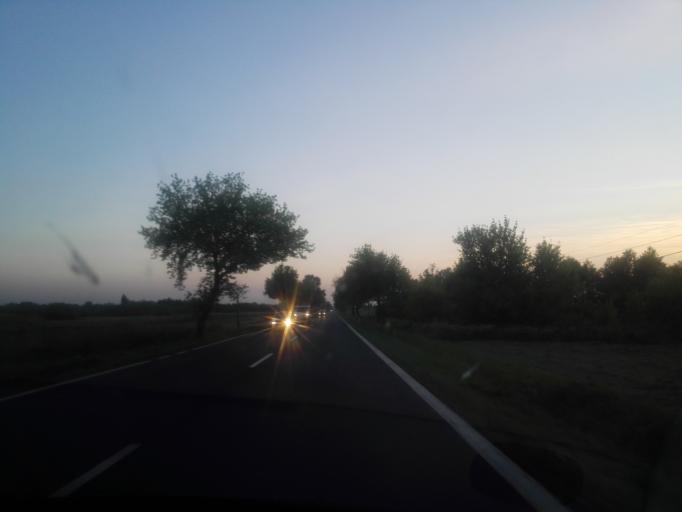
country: PL
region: Silesian Voivodeship
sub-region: Powiat zawiercianski
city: Szczekociny
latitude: 50.6321
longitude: 19.8689
